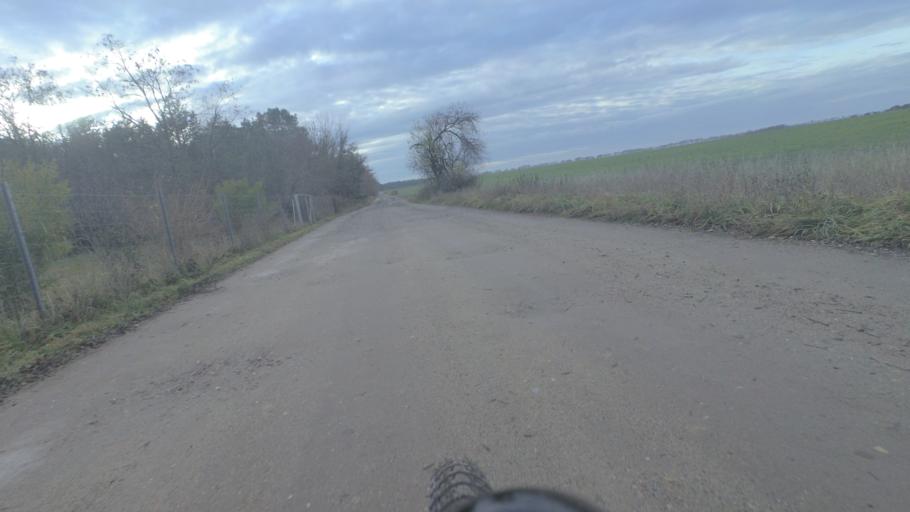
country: DE
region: Brandenburg
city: Rangsdorf
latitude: 52.2457
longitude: 13.3794
